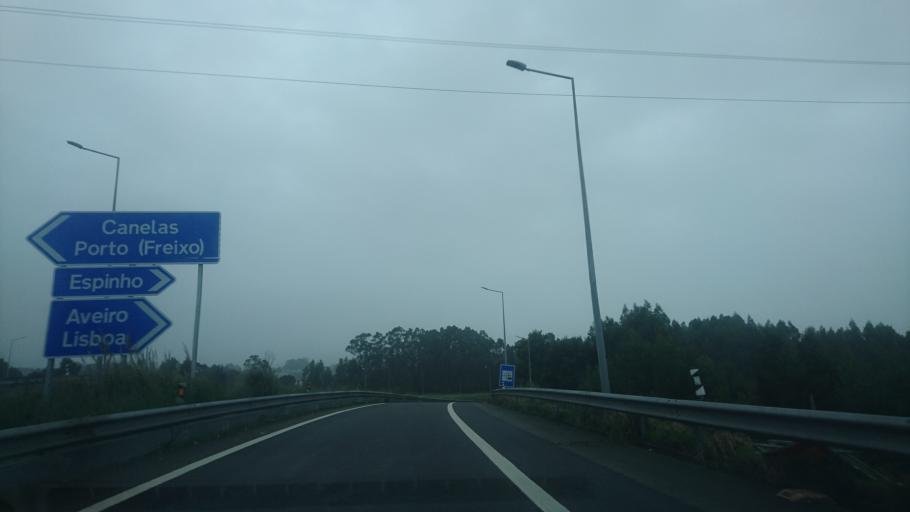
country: PT
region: Porto
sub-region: Vila Nova de Gaia
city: Gulpilhares
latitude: 41.0817
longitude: -8.6313
